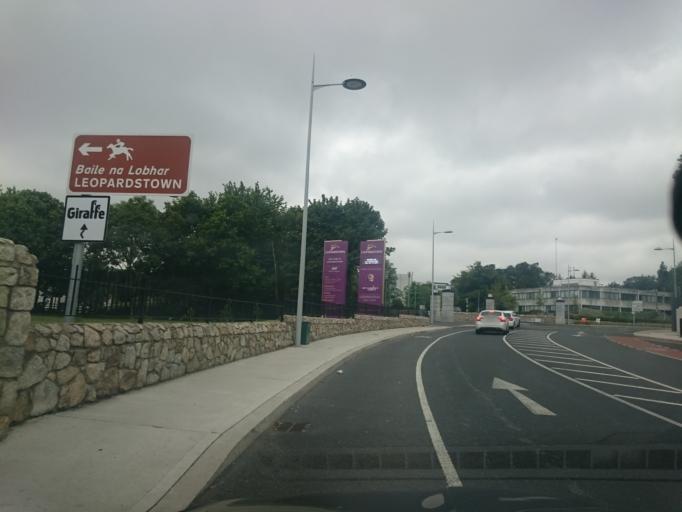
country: IE
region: Leinster
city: Foxrock
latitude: 53.2726
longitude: -6.1983
